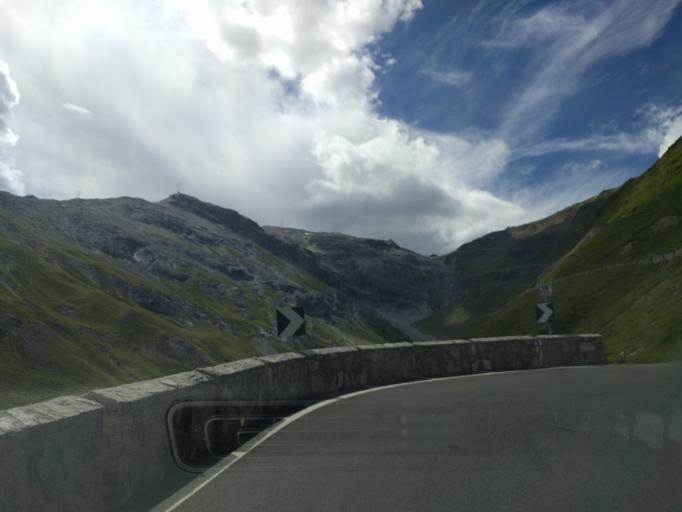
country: IT
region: Lombardy
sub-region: Provincia di Sondrio
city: Sant'Antonio
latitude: 46.5334
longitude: 10.4765
